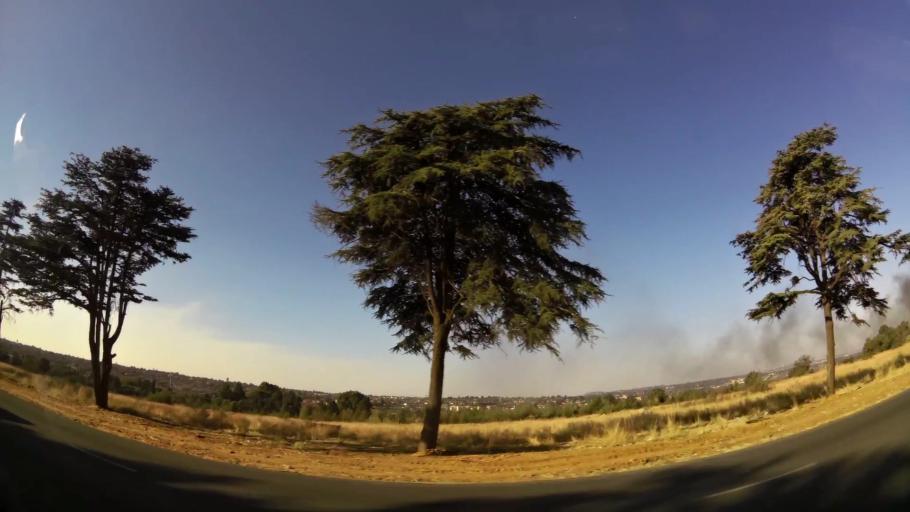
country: ZA
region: Gauteng
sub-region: City of Johannesburg Metropolitan Municipality
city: Roodepoort
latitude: -26.1697
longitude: 27.8730
